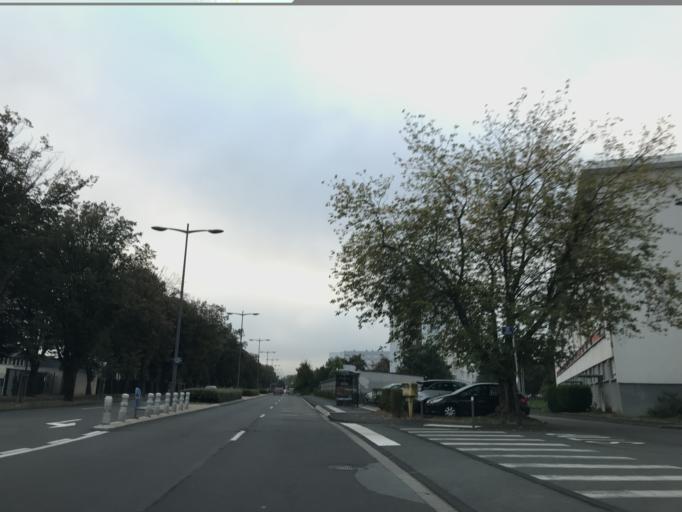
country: FR
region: Auvergne
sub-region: Departement du Puy-de-Dome
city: Gerzat
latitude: 45.8030
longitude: 3.1196
